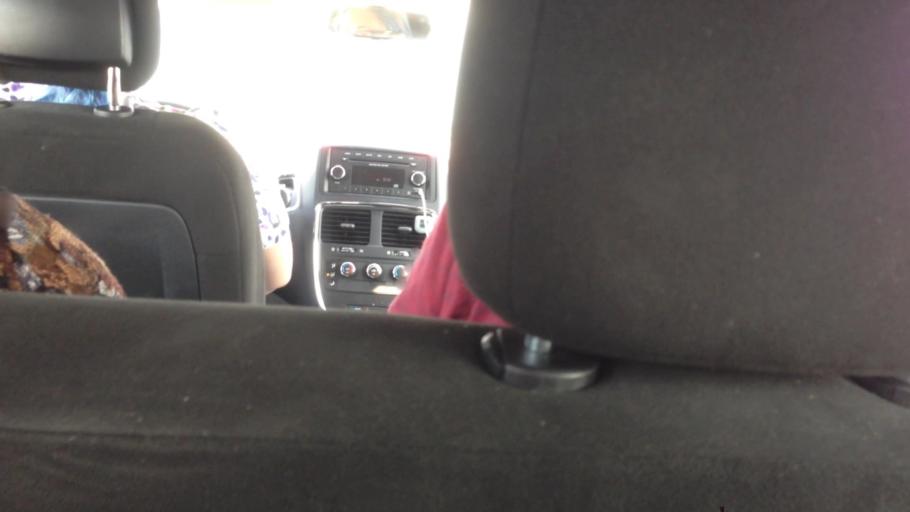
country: US
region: New York
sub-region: Ulster County
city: Lake Katrine
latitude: 41.9779
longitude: -73.9462
